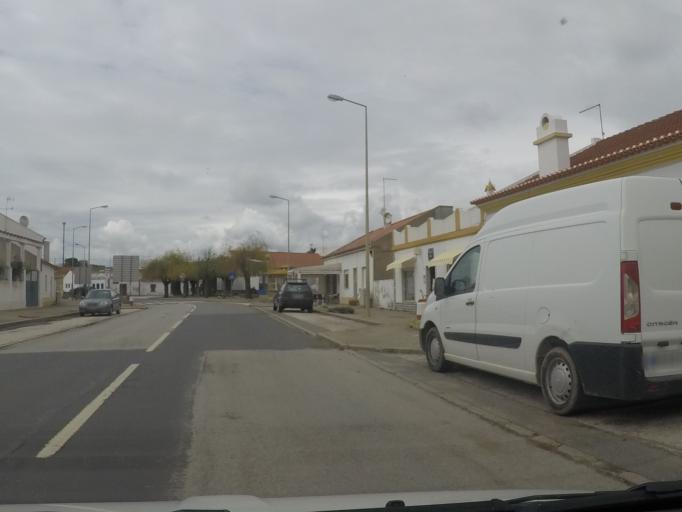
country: PT
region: Setubal
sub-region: Sines
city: Porto Covo
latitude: 37.8659
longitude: -8.7200
